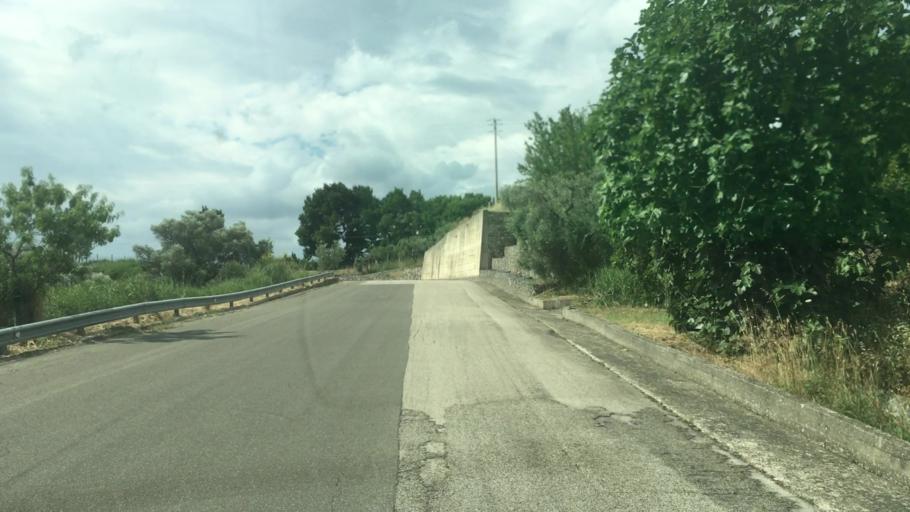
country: IT
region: Basilicate
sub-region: Provincia di Matera
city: San Mauro Forte
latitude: 40.4805
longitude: 16.2667
